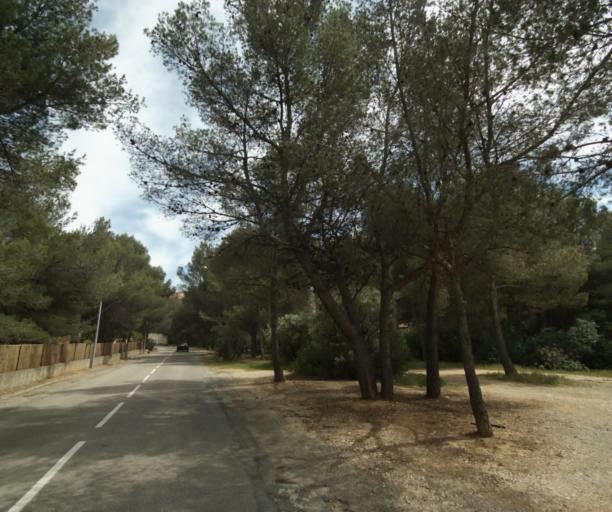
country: FR
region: Provence-Alpes-Cote d'Azur
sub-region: Departement des Bouches-du-Rhone
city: Rognac
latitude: 43.4781
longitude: 5.2405
